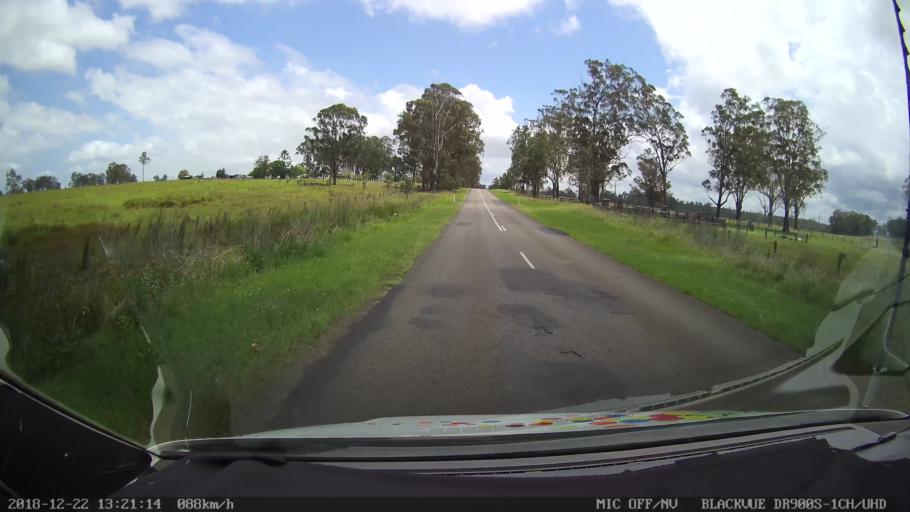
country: AU
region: New South Wales
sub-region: Clarence Valley
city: Coutts Crossing
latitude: -29.7748
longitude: 152.9222
